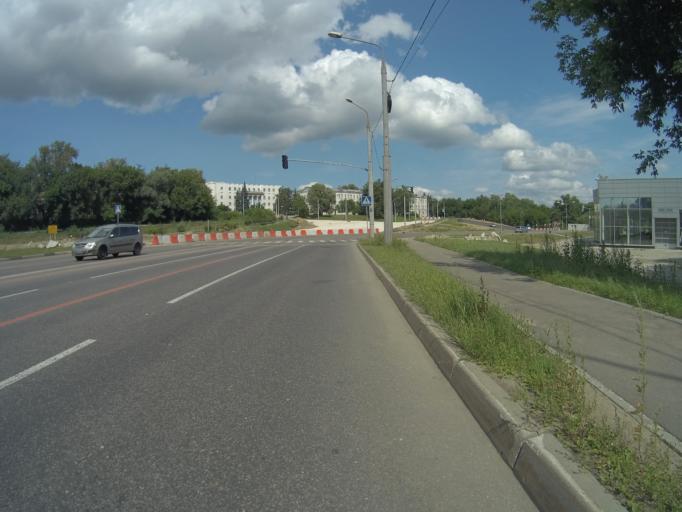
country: RU
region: Vladimir
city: Vladimir
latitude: 56.1334
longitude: 40.4045
